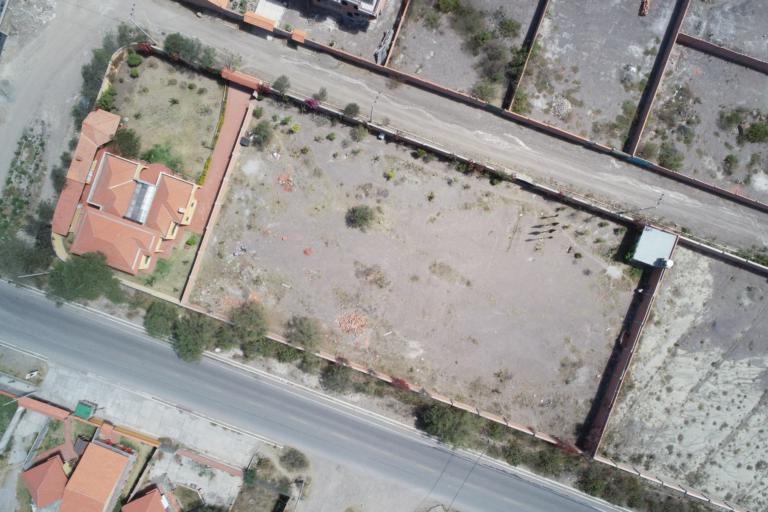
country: BO
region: La Paz
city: La Paz
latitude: -16.6496
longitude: -68.0377
